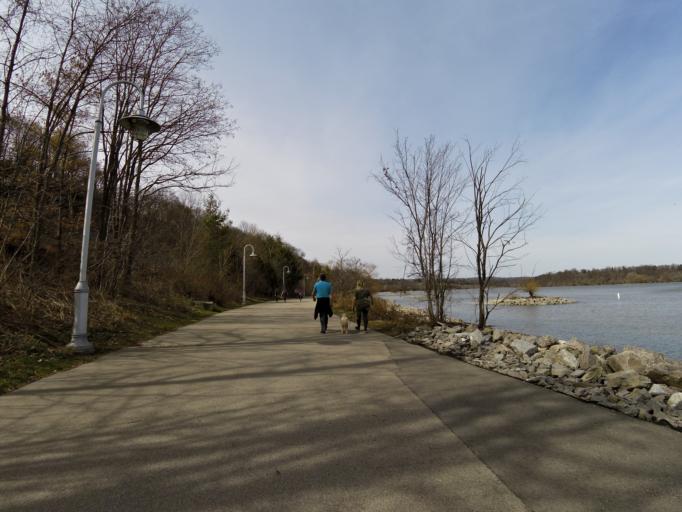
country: CA
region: Ontario
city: Hamilton
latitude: 43.2734
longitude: -79.8858
